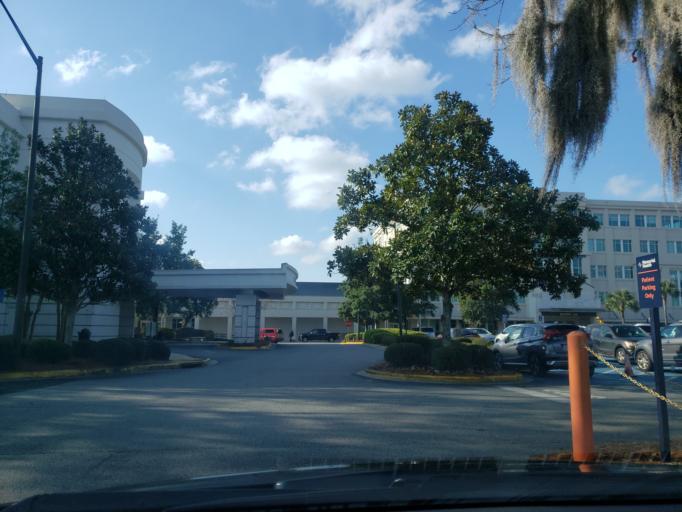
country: US
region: Georgia
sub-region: Chatham County
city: Thunderbolt
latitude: 32.0320
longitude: -81.0876
